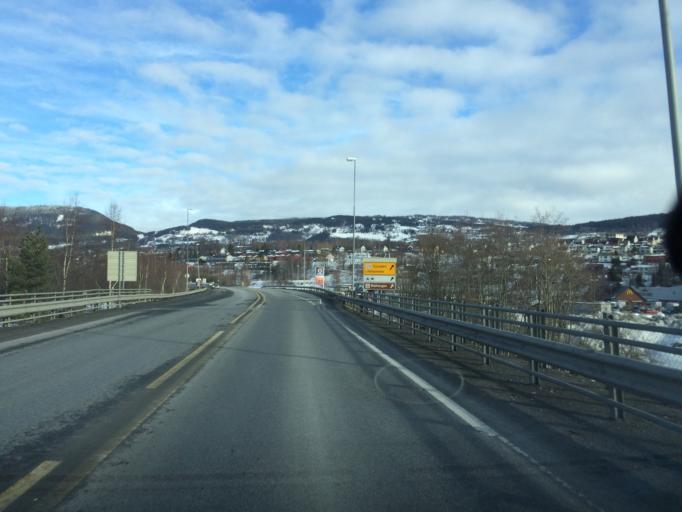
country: NO
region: Oppland
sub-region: Lillehammer
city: Lillehammer
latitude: 61.1136
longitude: 10.4448
